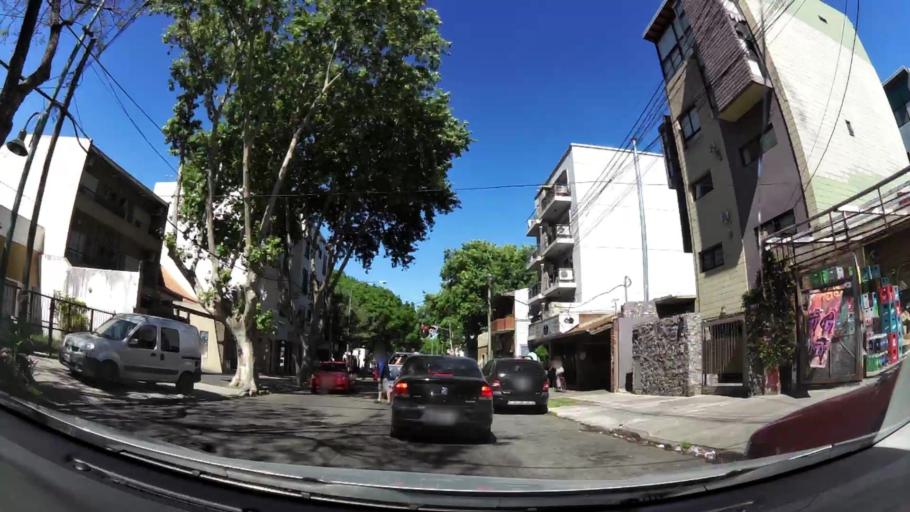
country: AR
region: Buenos Aires
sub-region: Partido de Vicente Lopez
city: Olivos
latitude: -34.5431
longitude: -58.4937
